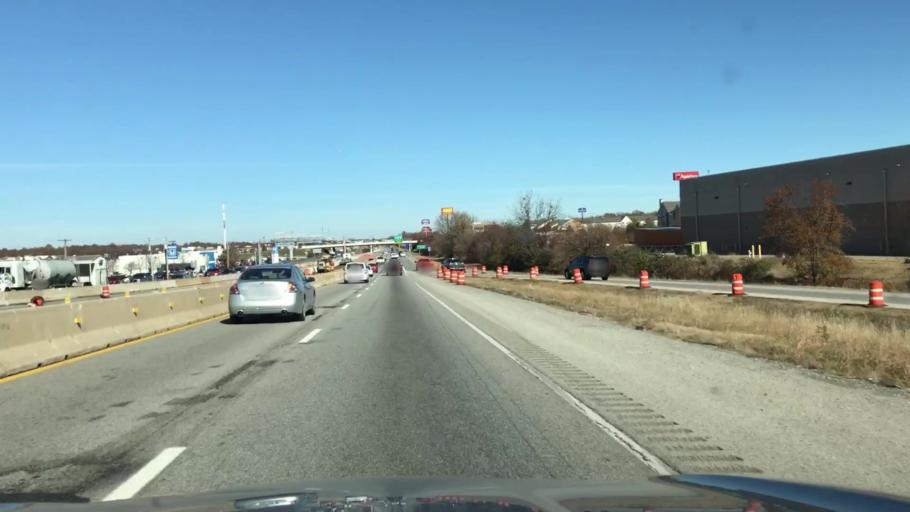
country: US
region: Arkansas
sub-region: Benton County
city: Bentonville
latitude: 36.3371
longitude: -94.1827
